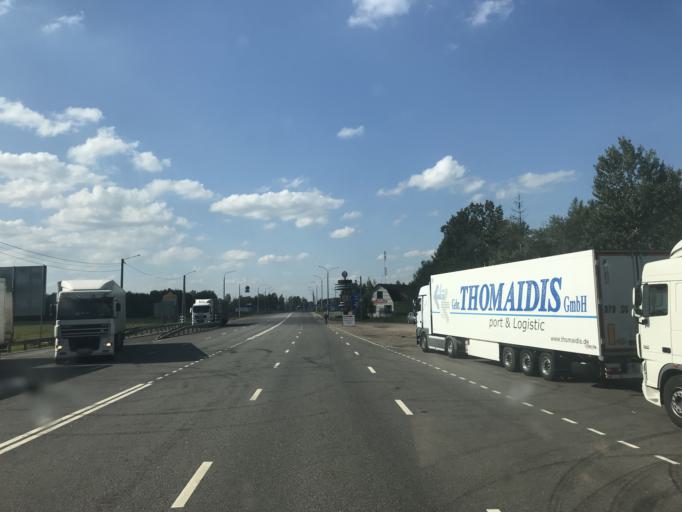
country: RU
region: Smolensk
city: Rudnya
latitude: 54.9884
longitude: 30.9545
